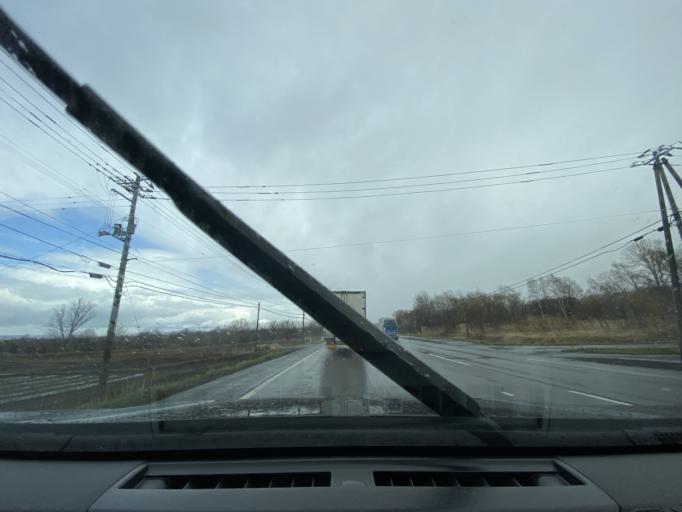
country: JP
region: Hokkaido
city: Fukagawa
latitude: 43.6721
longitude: 142.0170
